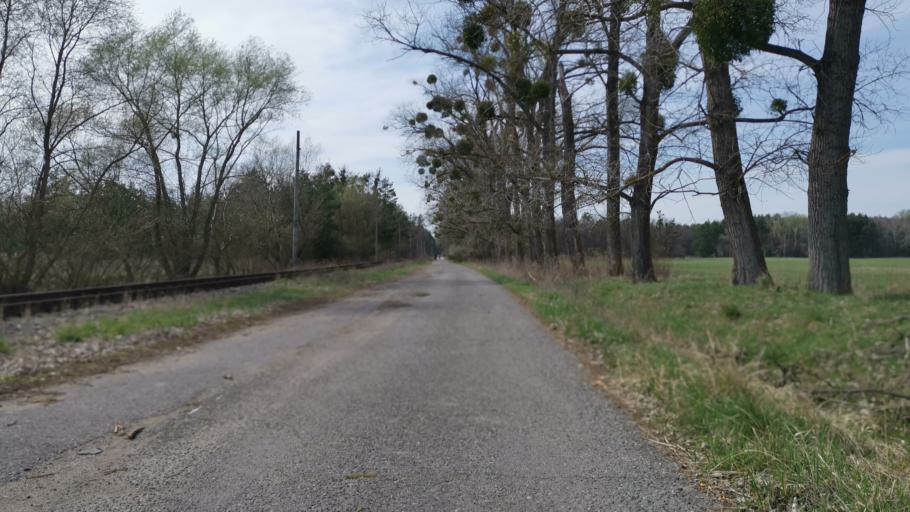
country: SK
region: Trnavsky
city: Gbely
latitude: 48.6644
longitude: 17.0656
